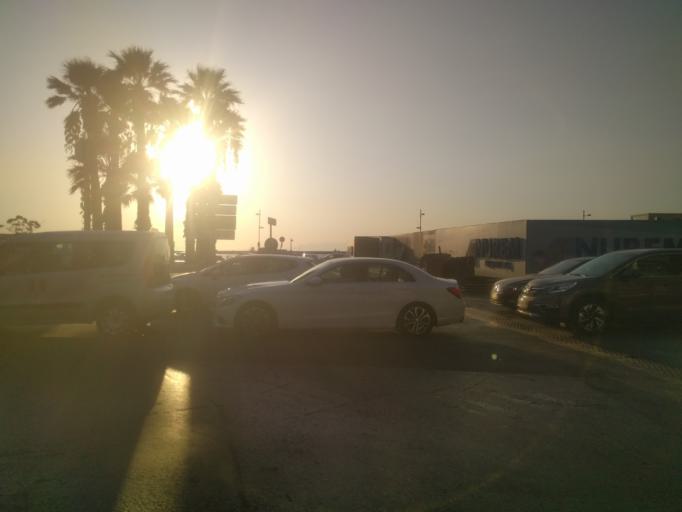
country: TR
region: Izmir
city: Izmir
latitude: 38.4246
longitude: 27.1321
